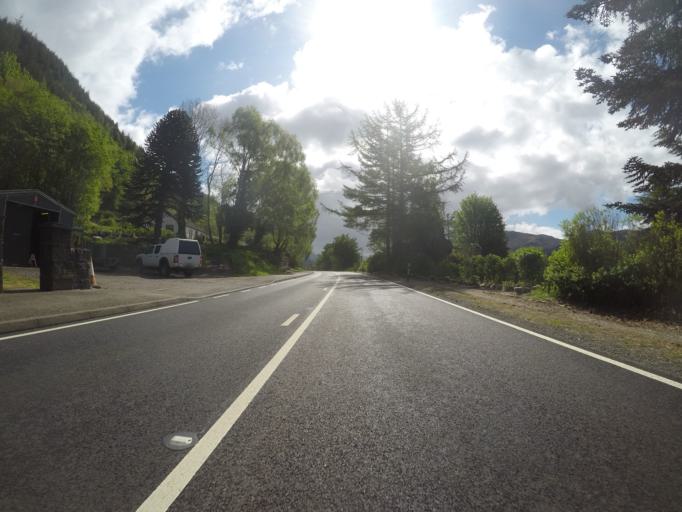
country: GB
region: Scotland
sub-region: Highland
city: Fort William
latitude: 57.2437
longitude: -5.4609
